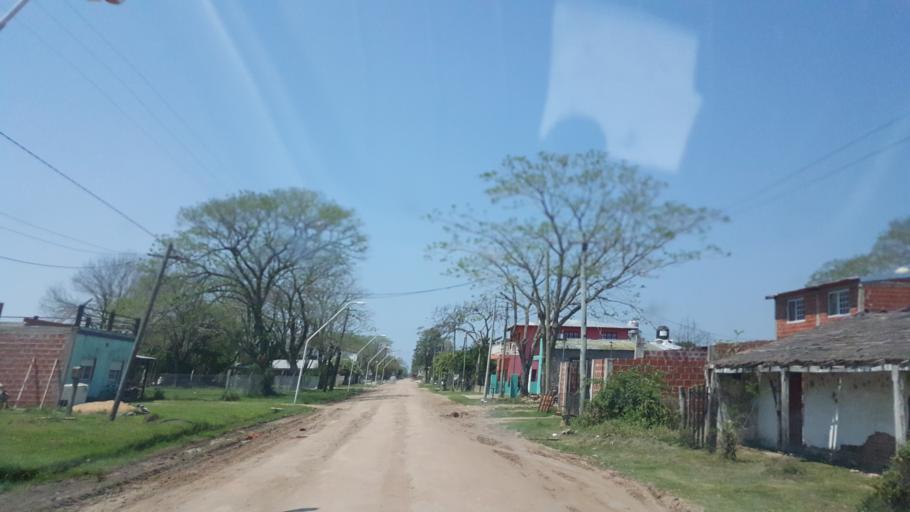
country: AR
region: Corrientes
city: Ita Ibate
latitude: -27.4260
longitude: -57.3409
